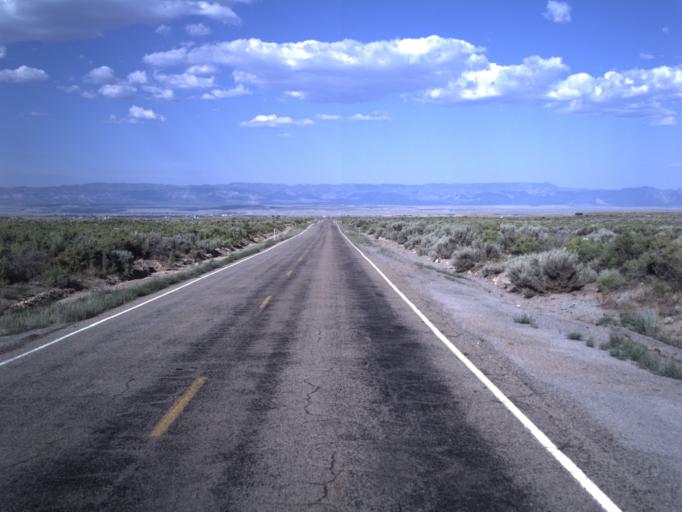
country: US
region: Utah
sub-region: Carbon County
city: Price
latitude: 39.4881
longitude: -110.8701
